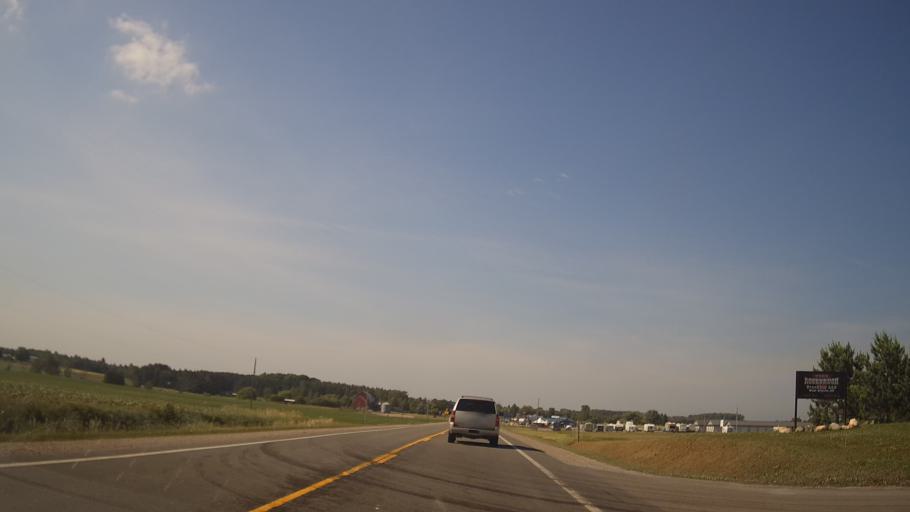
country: US
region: Michigan
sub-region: Ogemaw County
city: West Branch
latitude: 44.2709
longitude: -84.1257
